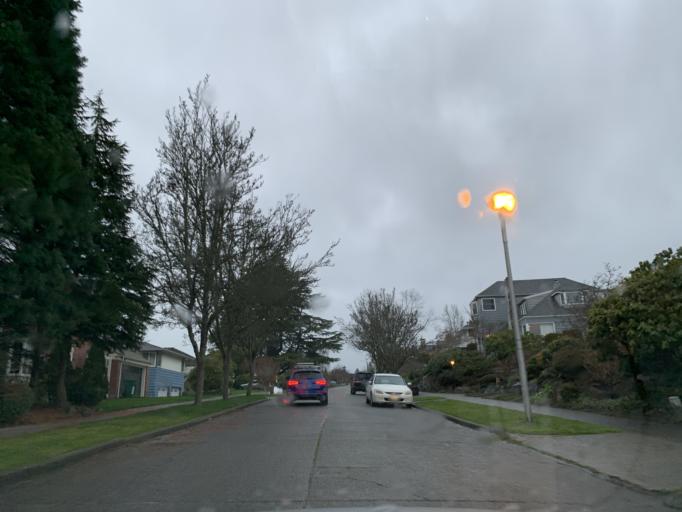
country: US
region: Washington
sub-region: King County
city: Yarrow Point
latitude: 47.6723
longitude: -122.2756
